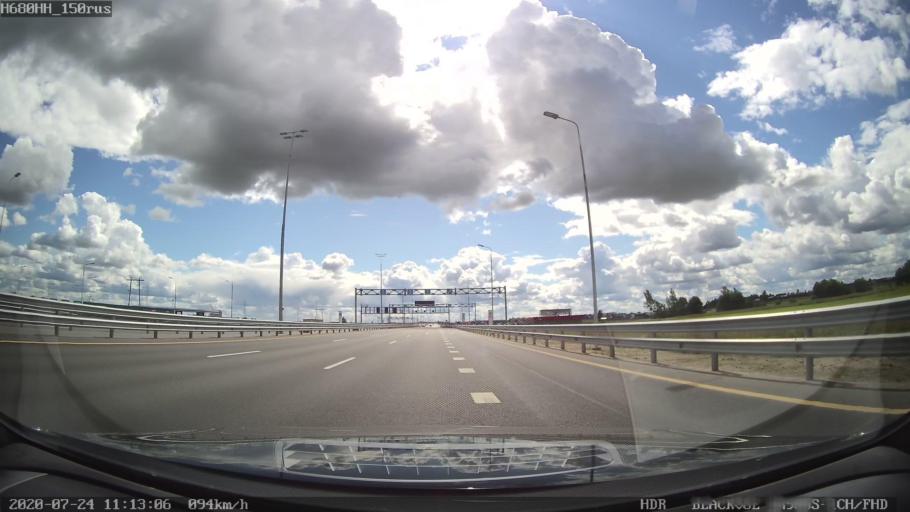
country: RU
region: Leningrad
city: Fedorovskoye
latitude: 59.7033
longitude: 30.5491
